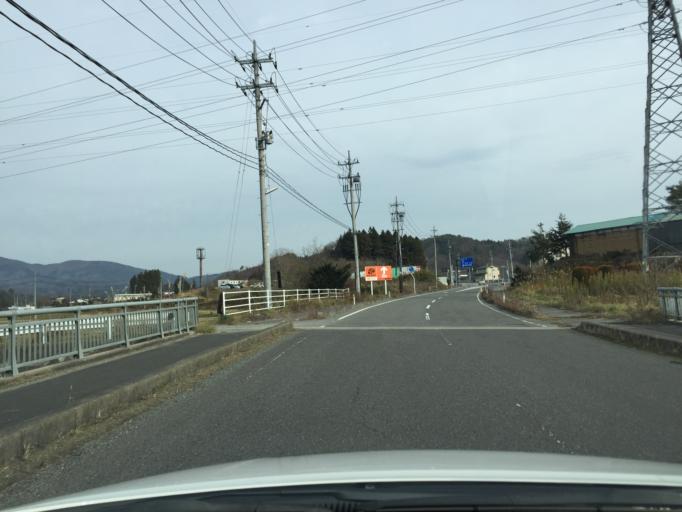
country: JP
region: Fukushima
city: Funehikimachi-funehiki
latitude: 37.4279
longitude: 140.5882
